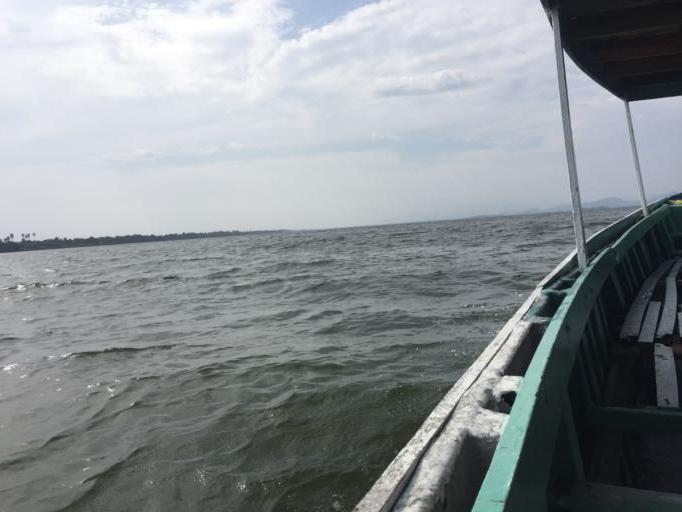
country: MX
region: Guerrero
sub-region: Coyuca de Benitez
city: Colonia Luces en el Mar
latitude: 16.9153
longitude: -99.9803
